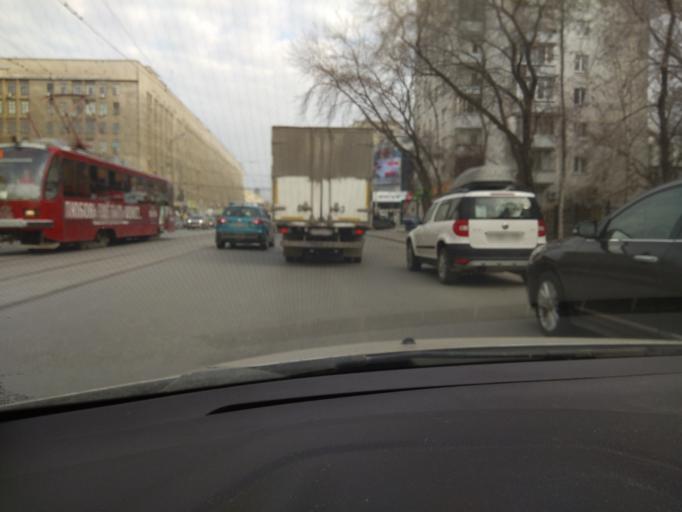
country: RU
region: Sverdlovsk
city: Yekaterinburg
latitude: 56.8354
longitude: 60.6223
